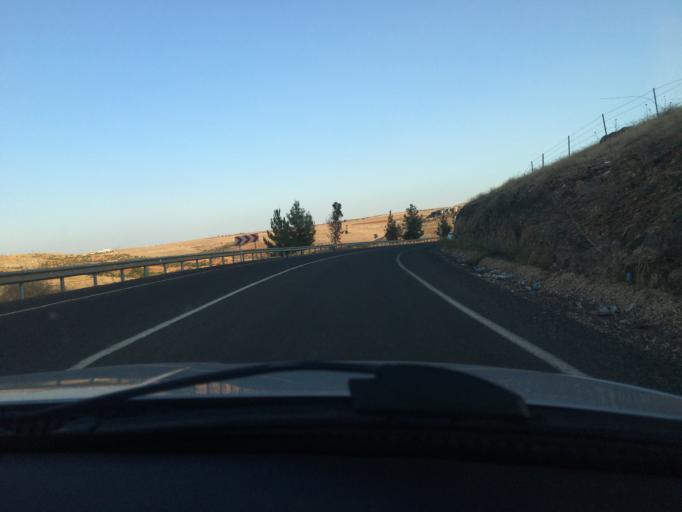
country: TR
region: Sanliurfa
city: Halfeti
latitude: 37.2266
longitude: 37.9574
